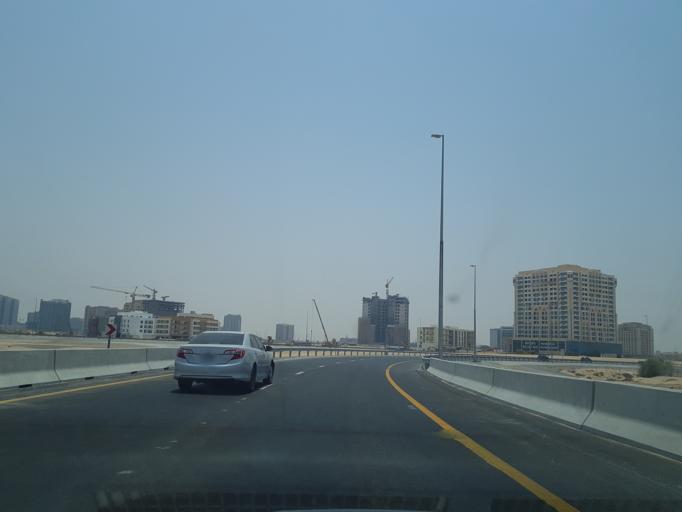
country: AE
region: Dubai
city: Dubai
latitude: 25.1032
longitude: 55.3753
